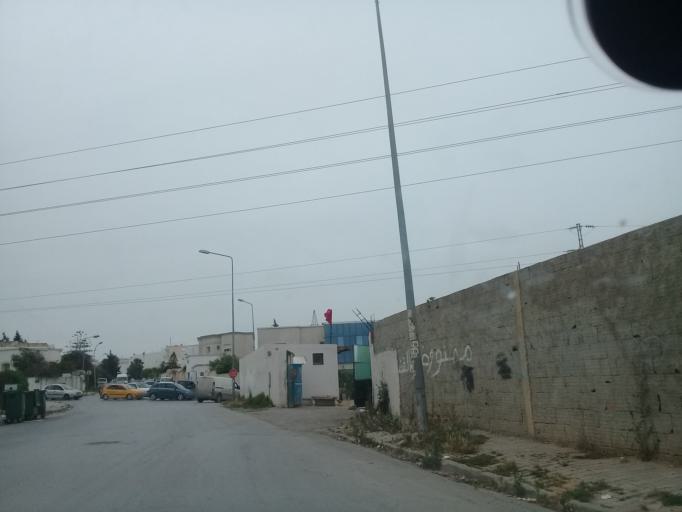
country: TN
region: Tunis
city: Tunis
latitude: 36.8495
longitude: 10.1537
